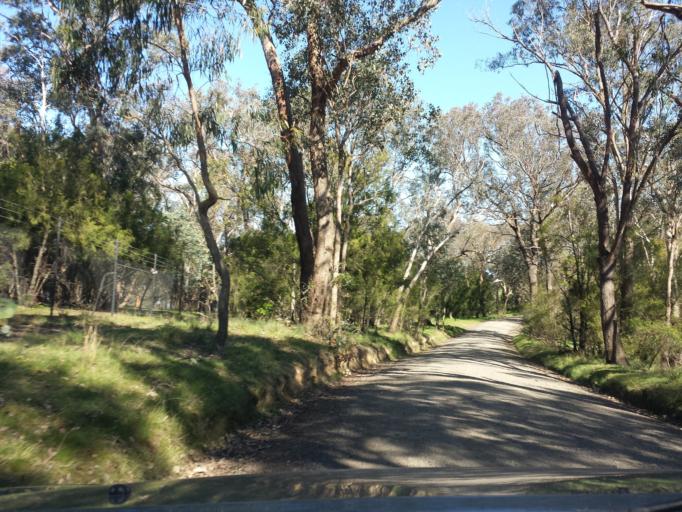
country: AU
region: Victoria
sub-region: Yarra Ranges
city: Yarra Glen
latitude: -37.6649
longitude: 145.3121
